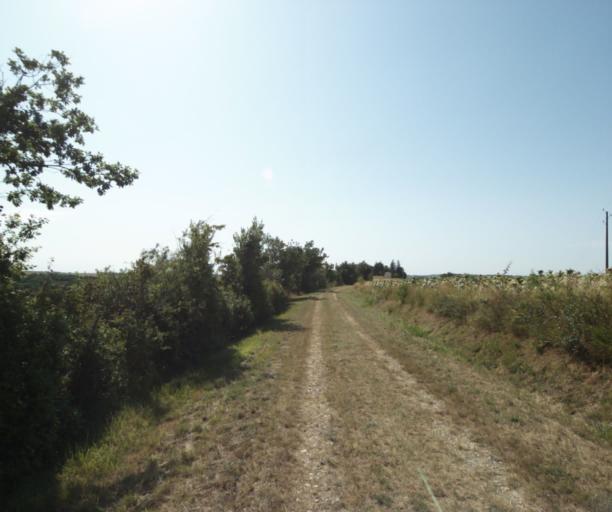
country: FR
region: Midi-Pyrenees
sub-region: Departement de la Haute-Garonne
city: Saint-Felix-Lauragais
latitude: 43.4389
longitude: 1.8387
